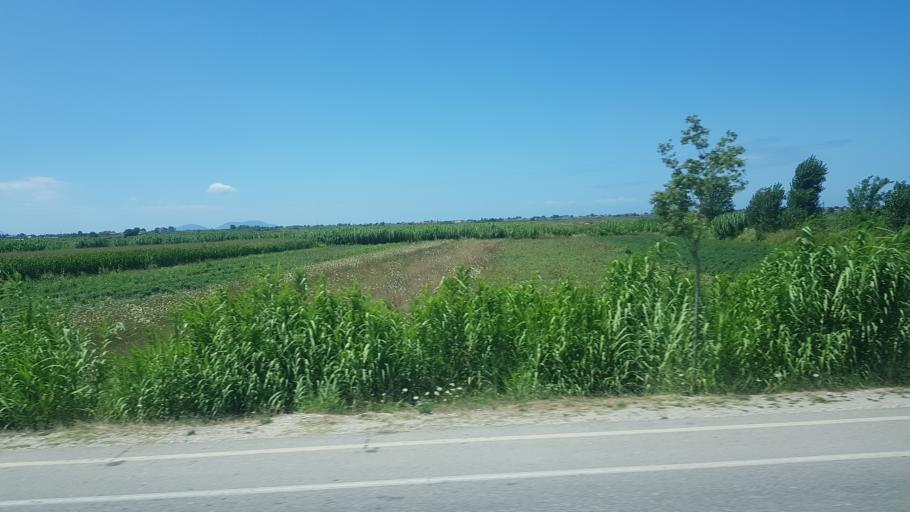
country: AL
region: Fier
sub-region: Rrethi i Fierit
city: Frakulla e Madhe
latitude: 40.6539
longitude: 19.4928
